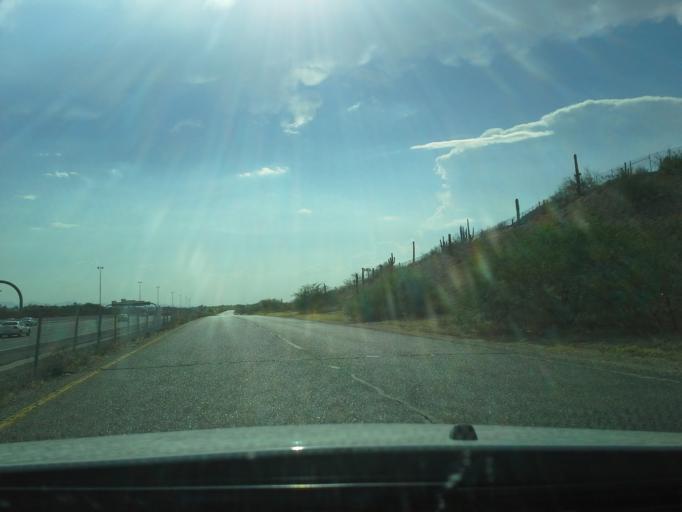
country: US
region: Arizona
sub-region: Maricopa County
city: Peoria
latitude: 33.6699
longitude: -112.1530
